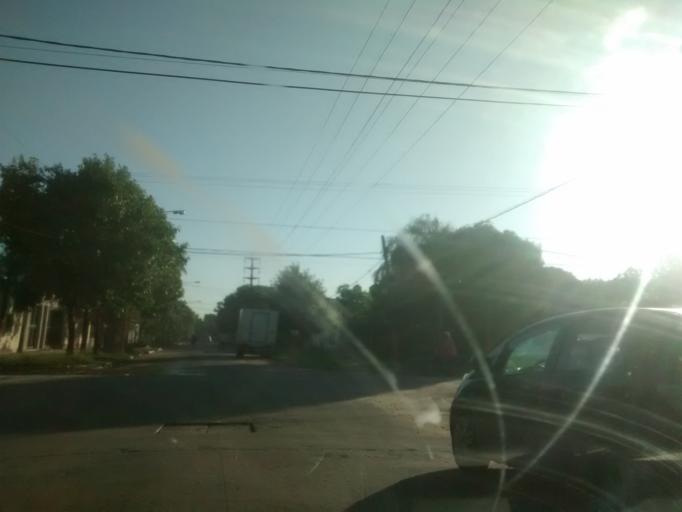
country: AR
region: Chaco
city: Resistencia
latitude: -27.4632
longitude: -58.9948
